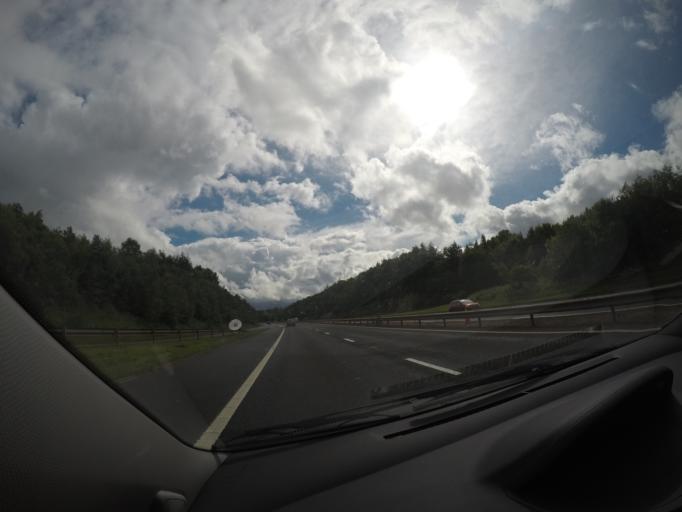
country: GB
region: Scotland
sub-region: North Lanarkshire
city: Glenboig
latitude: 55.8893
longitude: -4.0770
